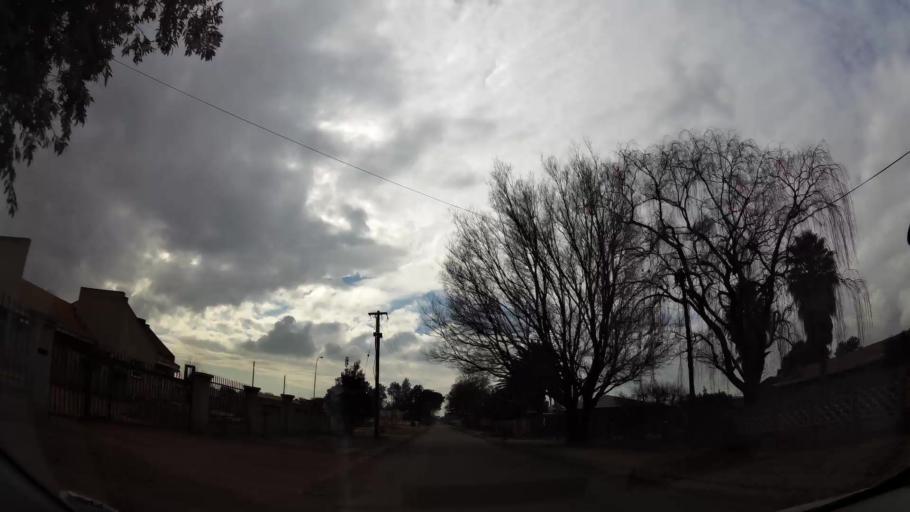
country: ZA
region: Gauteng
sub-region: Sedibeng District Municipality
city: Meyerton
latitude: -26.5896
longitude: 27.9954
